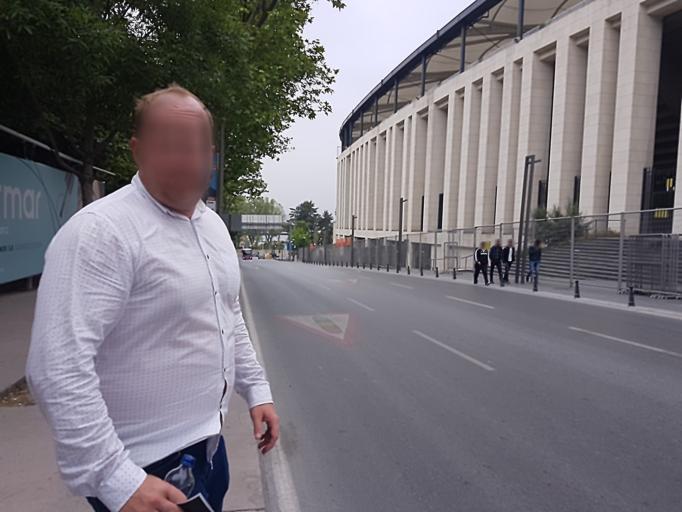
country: TR
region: Istanbul
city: Sisli
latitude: 41.0402
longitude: 28.9951
